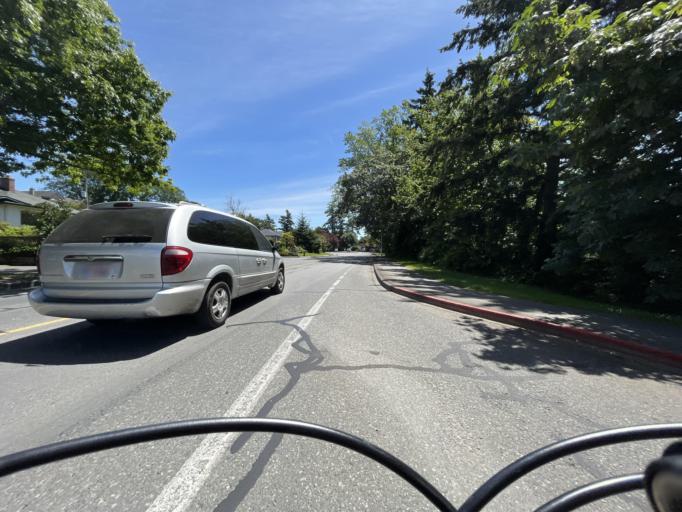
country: CA
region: British Columbia
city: Victoria
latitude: 48.4509
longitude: -123.4144
